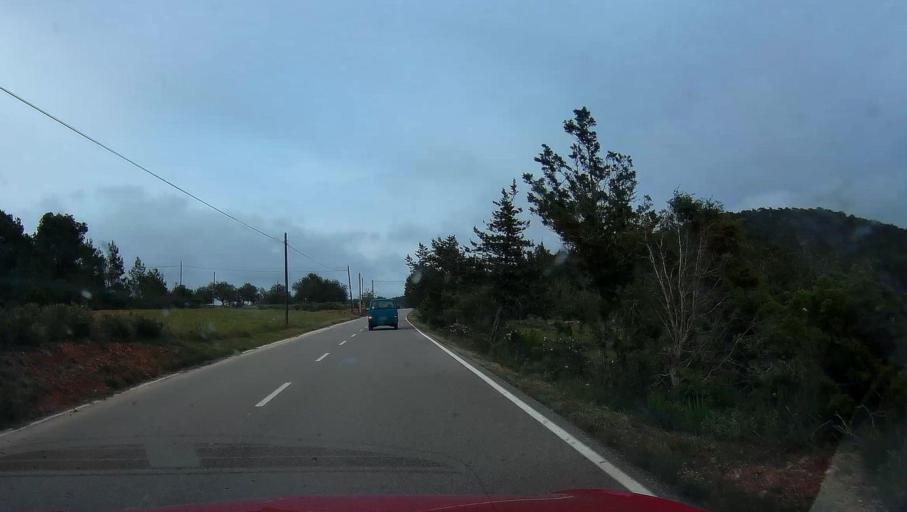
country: ES
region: Balearic Islands
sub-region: Illes Balears
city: Sant Antoni de Portmany
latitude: 39.0460
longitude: 1.4009
